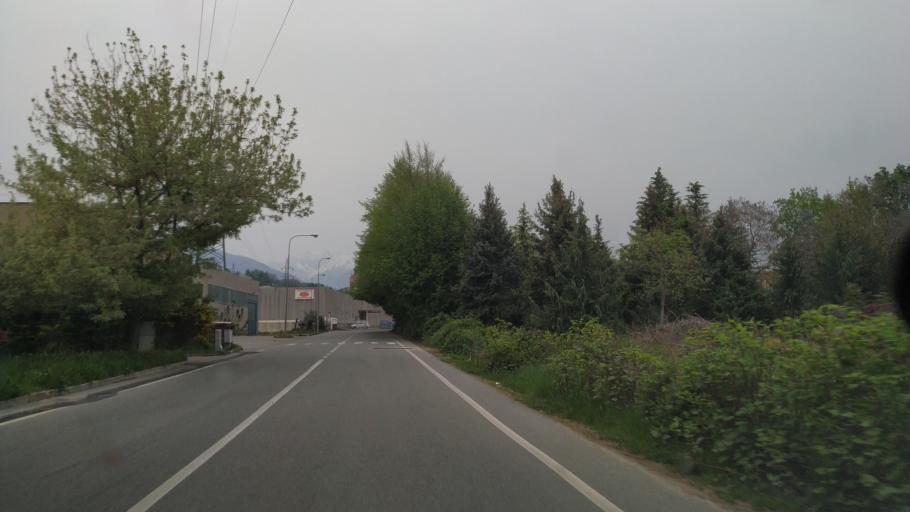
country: IT
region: Piedmont
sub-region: Provincia di Biella
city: Biella
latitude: 45.5532
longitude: 8.0439
